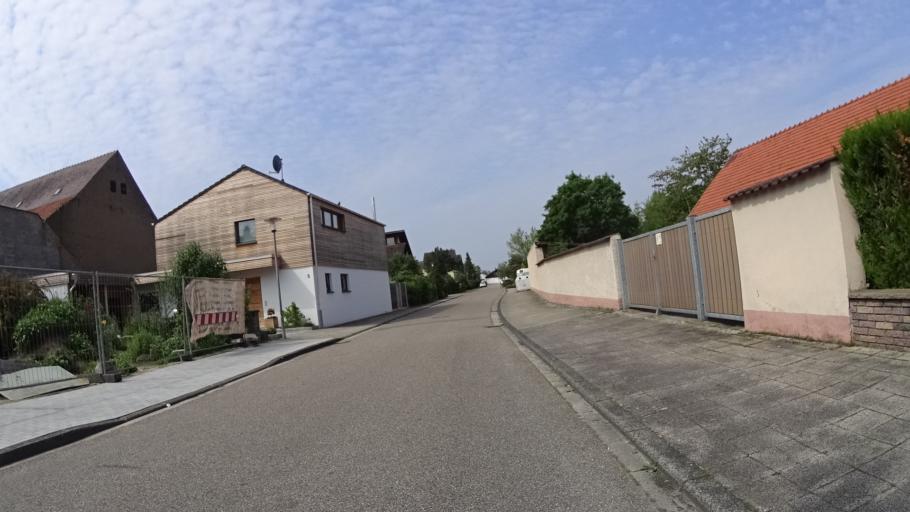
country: DE
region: Baden-Wuerttemberg
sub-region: Karlsruhe Region
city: Graben-Neudorf
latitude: 49.1550
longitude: 8.4755
